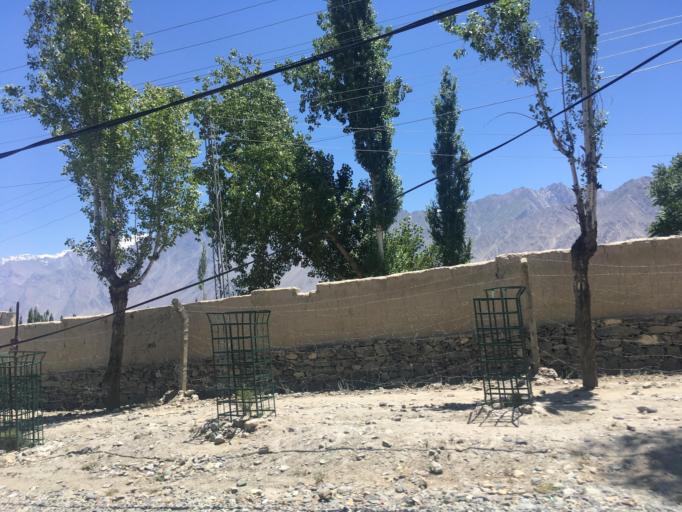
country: PK
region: Gilgit-Baltistan
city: Skardu
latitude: 35.3115
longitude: 75.5362
